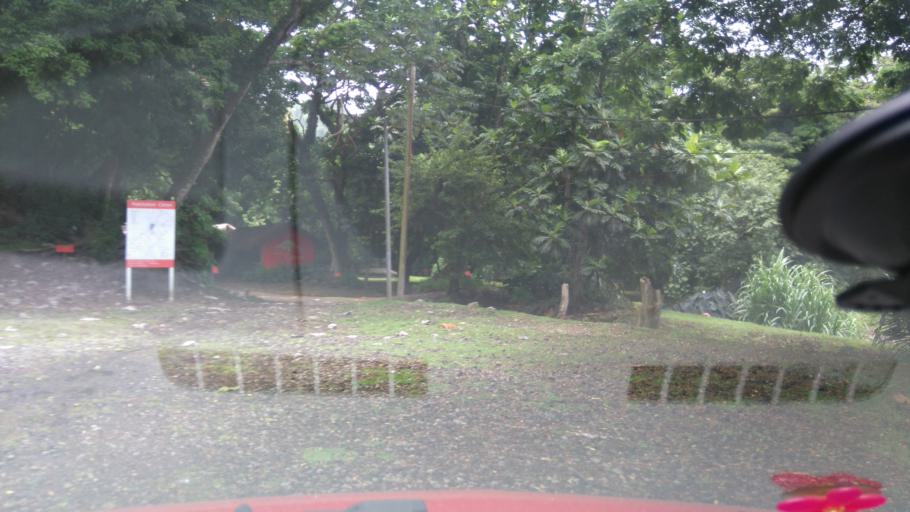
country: MQ
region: Martinique
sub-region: Martinique
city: Saint-Pierre
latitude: 14.8315
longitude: -61.2229
